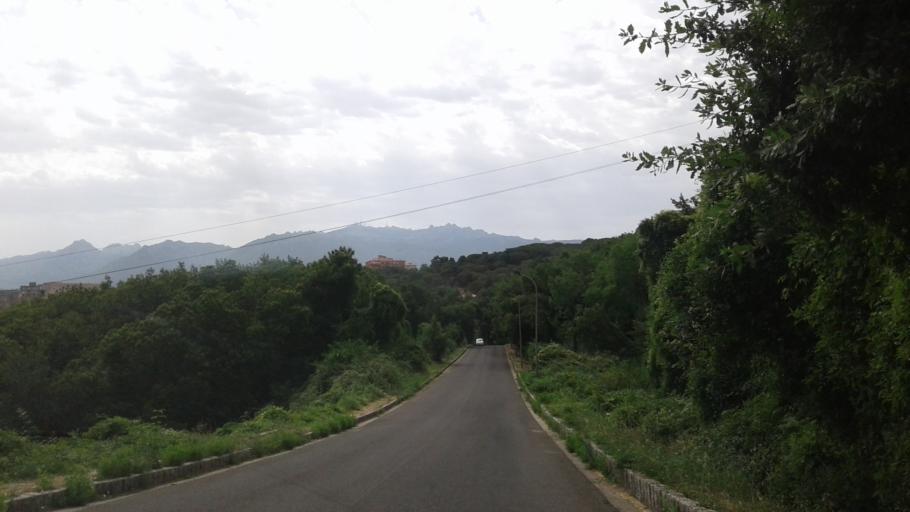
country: IT
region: Sardinia
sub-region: Provincia di Olbia-Tempio
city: Tempio Pausania
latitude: 40.9021
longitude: 9.0925
